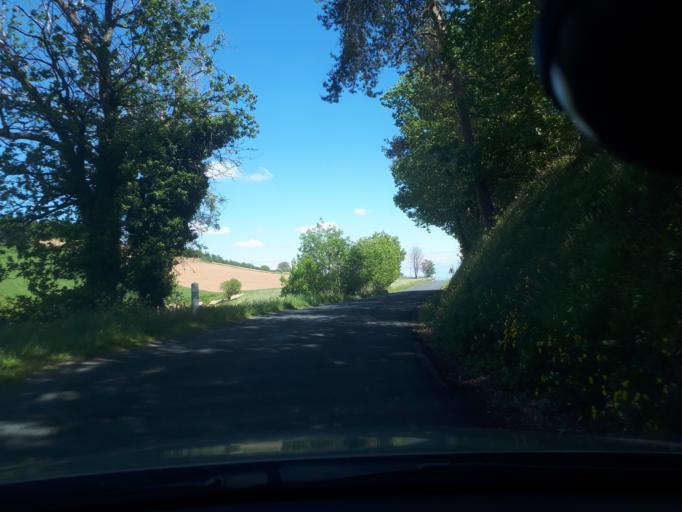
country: FR
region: Rhone-Alpes
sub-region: Departement du Rhone
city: Saint-Didier-sous-Riverie
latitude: 45.6396
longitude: 4.6122
